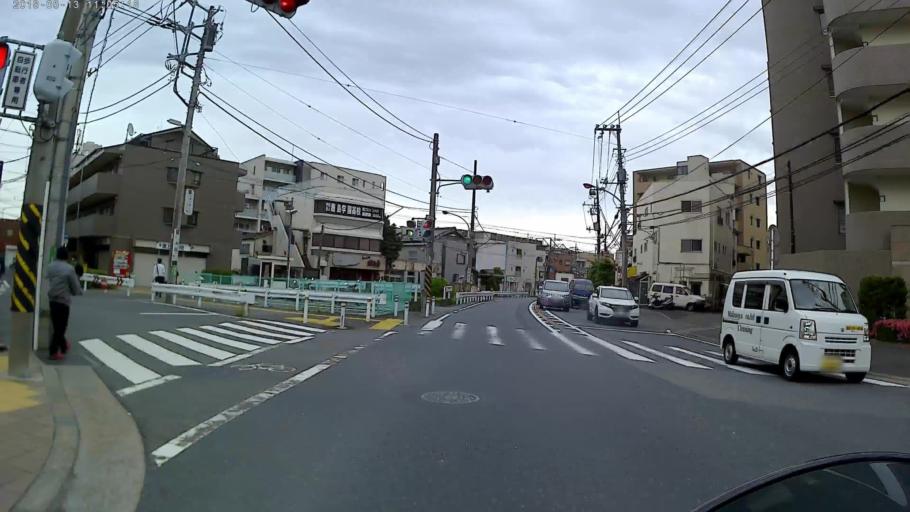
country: JP
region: Tokyo
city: Chofugaoka
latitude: 35.5972
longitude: 139.6125
